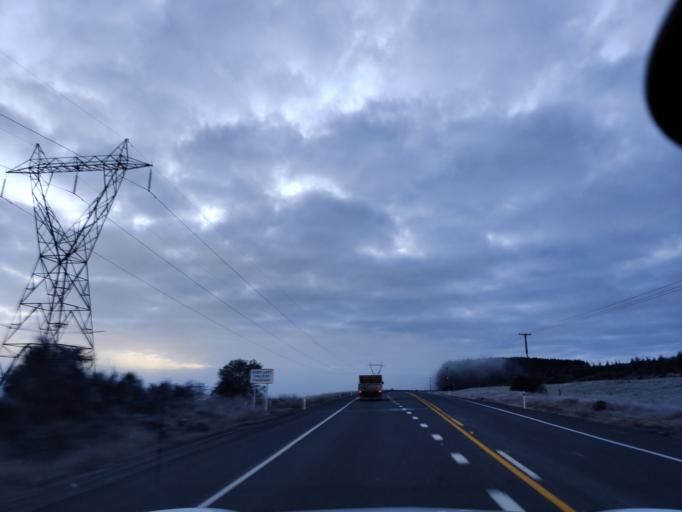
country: NZ
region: Waikato
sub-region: South Waikato District
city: Tokoroa
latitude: -38.3965
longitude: 176.0342
